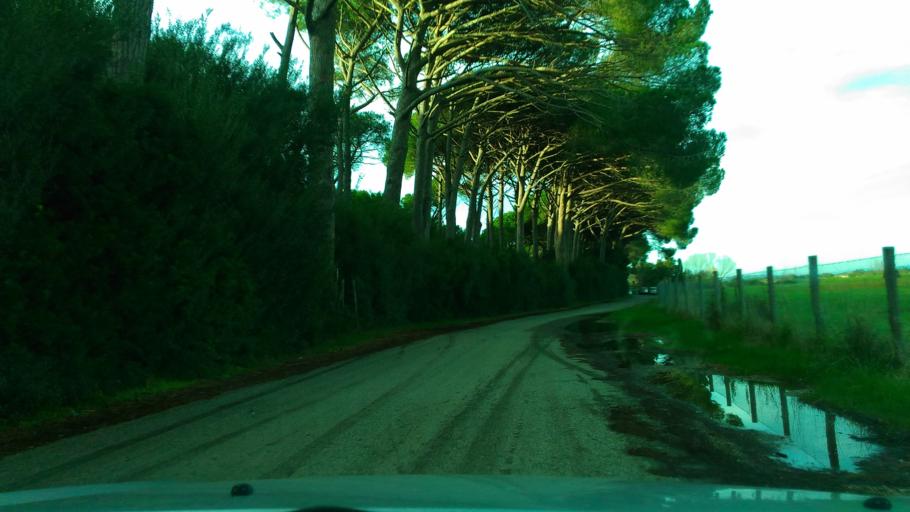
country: IT
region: Tuscany
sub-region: Provincia di Livorno
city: Cecina
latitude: 43.2791
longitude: 10.5146
